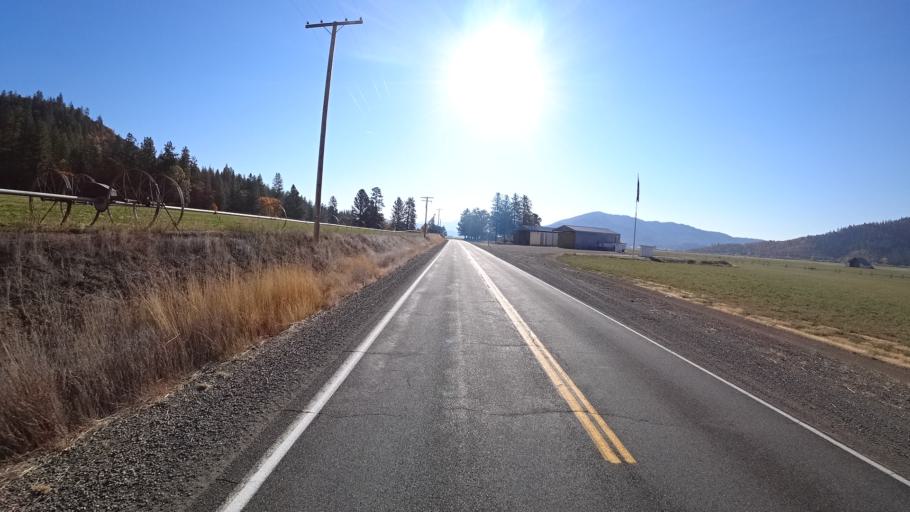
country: US
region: California
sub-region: Siskiyou County
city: Yreka
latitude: 41.6376
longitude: -122.9087
